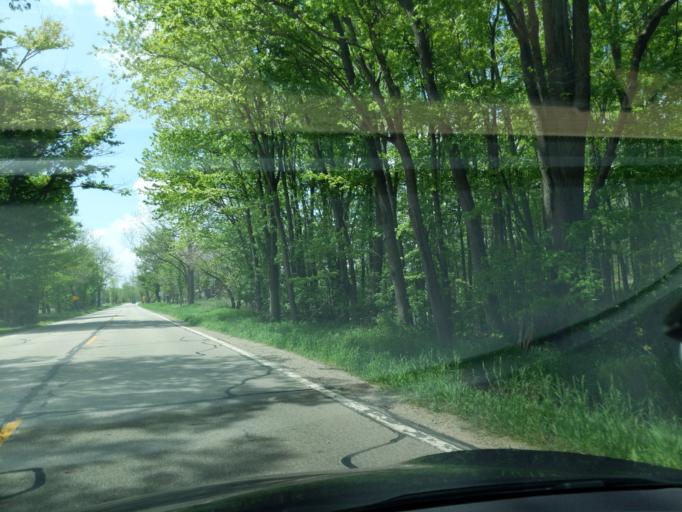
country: US
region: Michigan
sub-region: Ingham County
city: Stockbridge
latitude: 42.4968
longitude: -84.1164
